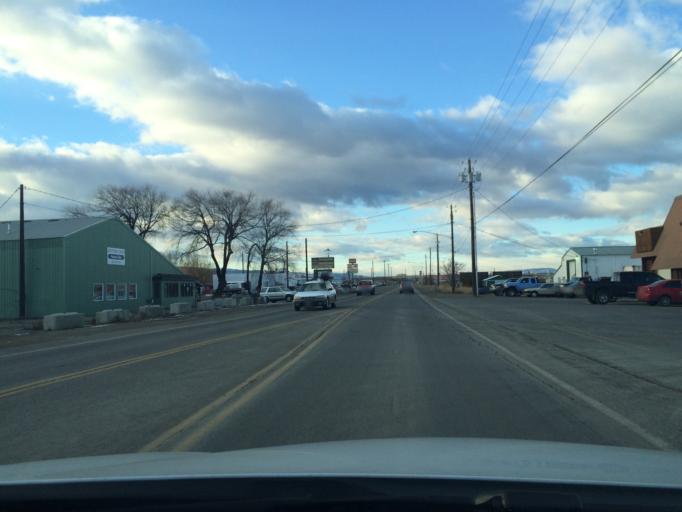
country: US
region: Washington
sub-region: Kittitas County
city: Ellensburg
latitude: 47.0067
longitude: -120.5693
